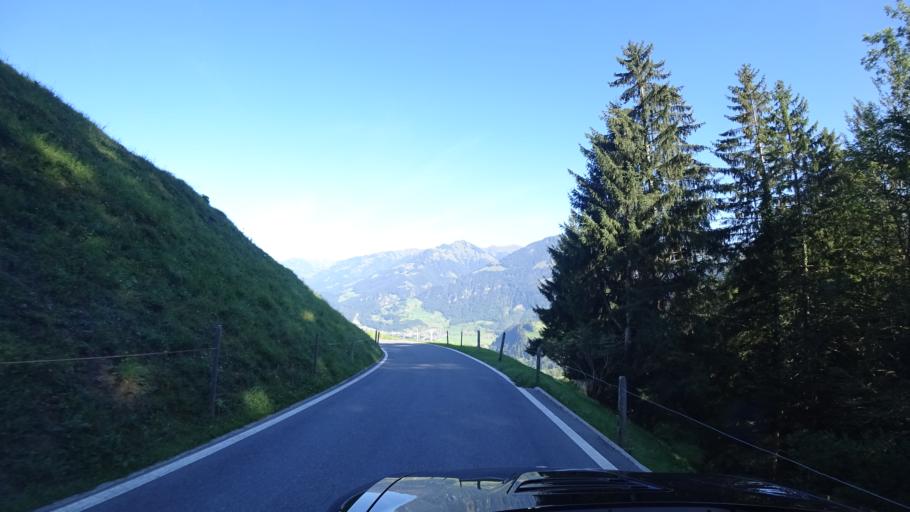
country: CH
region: Obwalden
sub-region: Obwalden
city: Giswil
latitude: 46.8333
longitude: 8.1349
